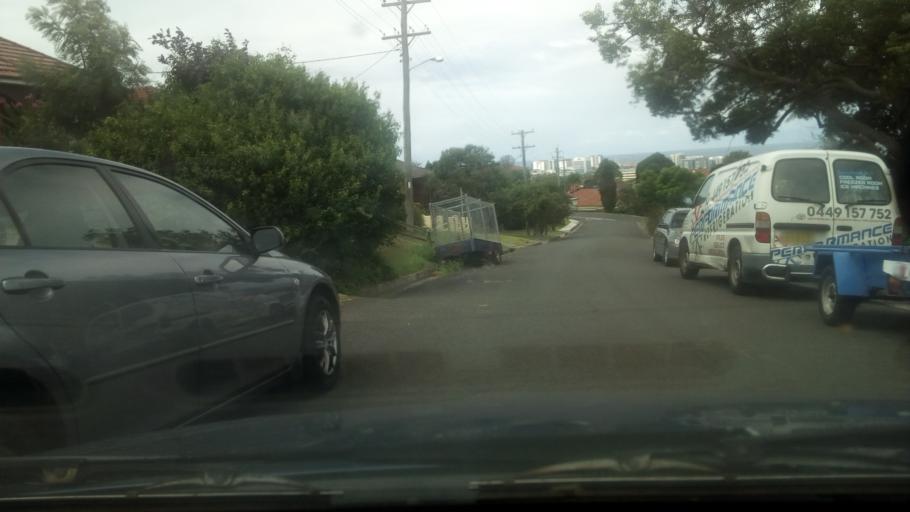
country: AU
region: New South Wales
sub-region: Wollongong
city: Mangerton
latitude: -34.4304
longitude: 150.8811
